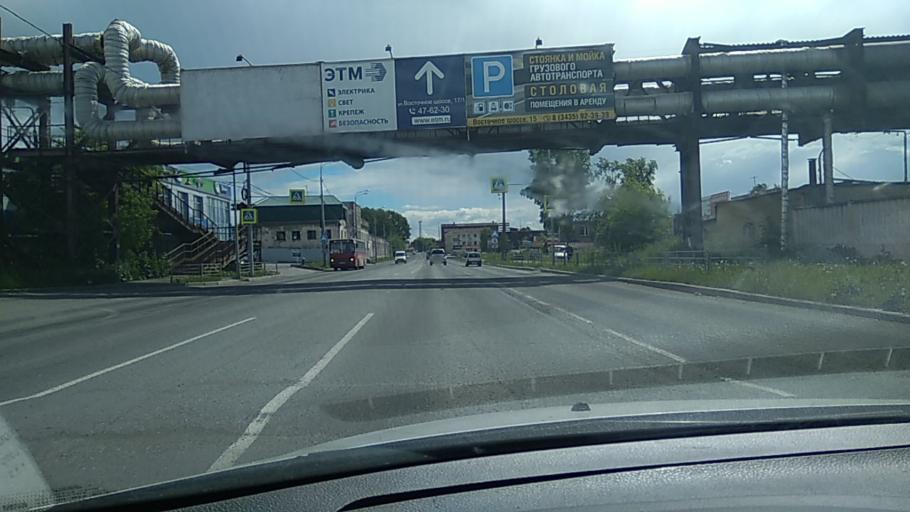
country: RU
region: Sverdlovsk
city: Nizhniy Tagil
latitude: 57.9182
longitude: 59.9894
